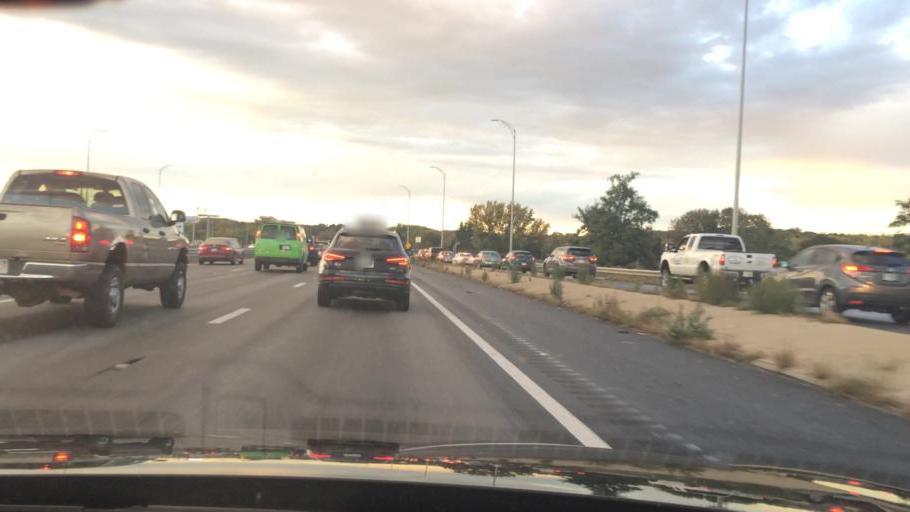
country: US
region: Massachusetts
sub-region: Essex County
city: North Andover
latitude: 42.7113
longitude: -71.1370
